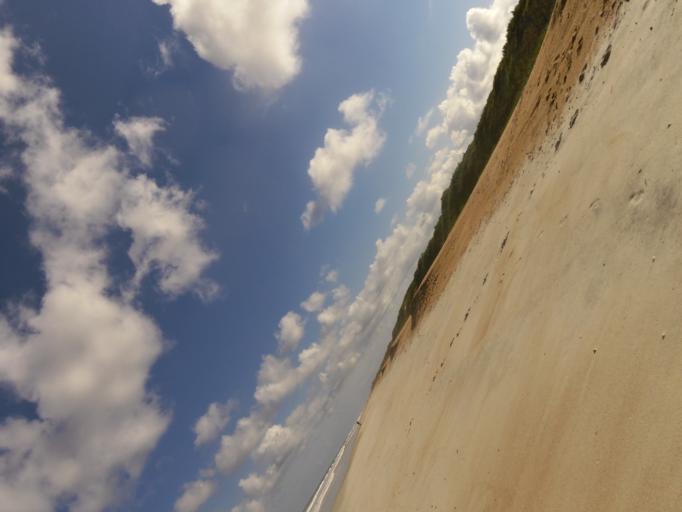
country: US
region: Florida
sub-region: Saint Johns County
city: Palm Valley
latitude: 30.0682
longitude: -81.3717
